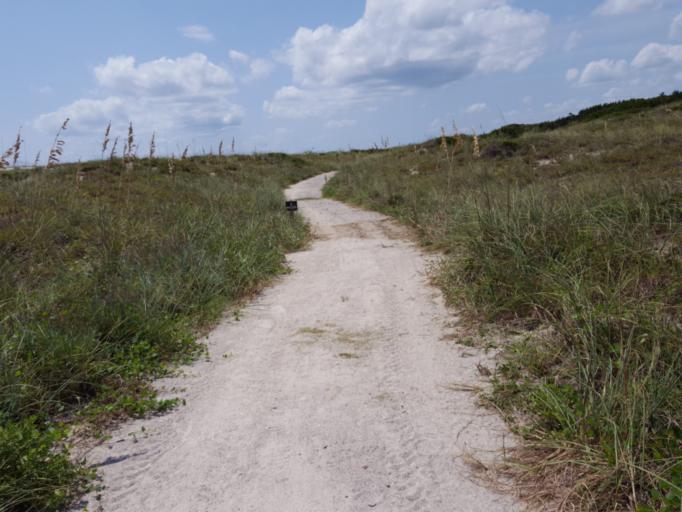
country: US
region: North Carolina
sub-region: Carteret County
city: Beaufort
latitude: 34.6949
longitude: -76.6782
